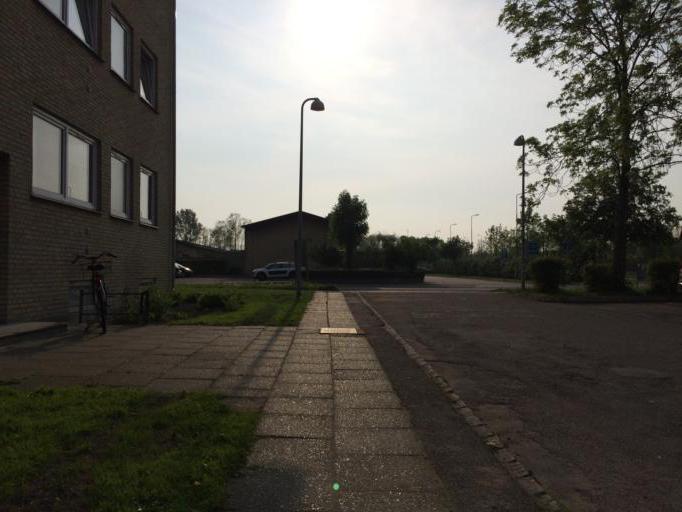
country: DK
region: Capital Region
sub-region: Hoje-Taastrup Kommune
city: Taastrup
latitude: 55.6465
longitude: 12.2864
